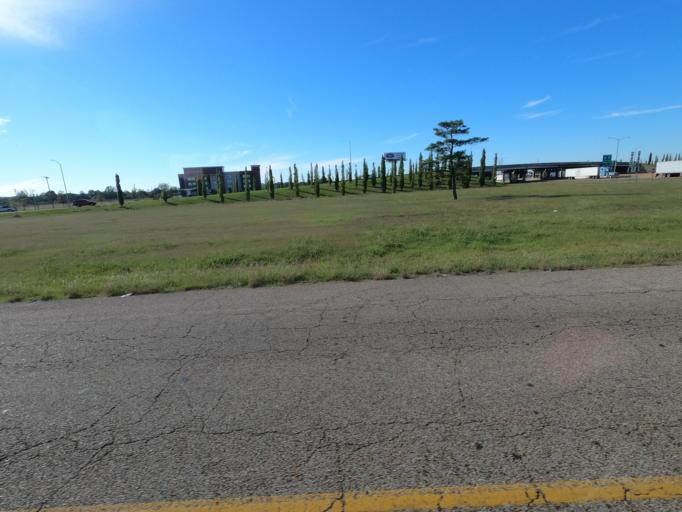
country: US
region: Arkansas
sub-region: Crittenden County
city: West Memphis
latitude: 35.1635
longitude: -90.1747
